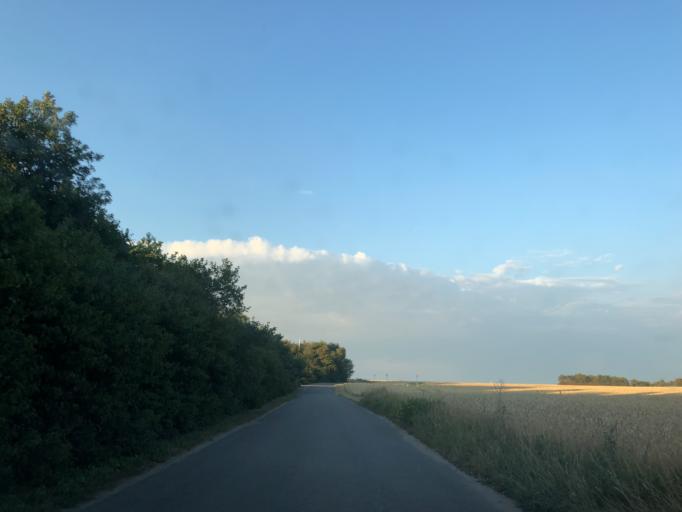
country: DK
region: Central Jutland
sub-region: Holstebro Kommune
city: Holstebro
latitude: 56.3681
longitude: 8.6776
